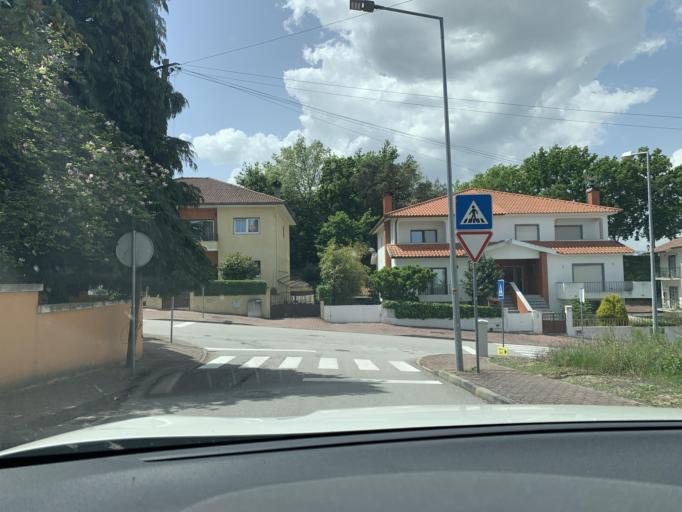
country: PT
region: Viseu
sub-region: Mangualde
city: Mangualde
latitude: 40.6064
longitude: -7.7675
